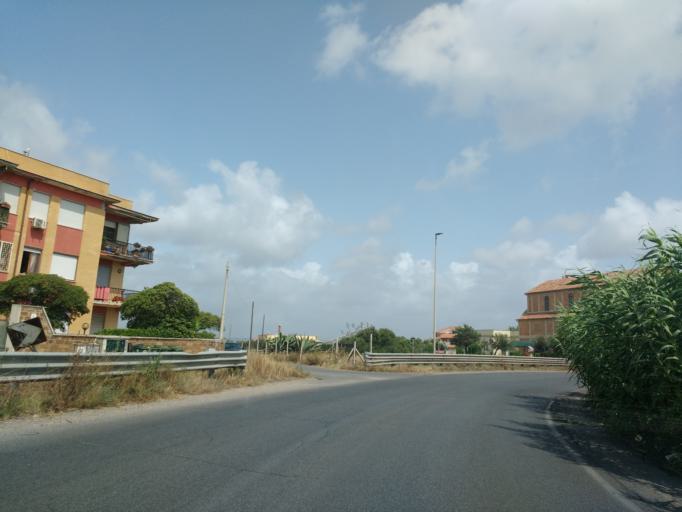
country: IT
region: Latium
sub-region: Citta metropolitana di Roma Capitale
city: Ardea
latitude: 41.5995
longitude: 12.4877
